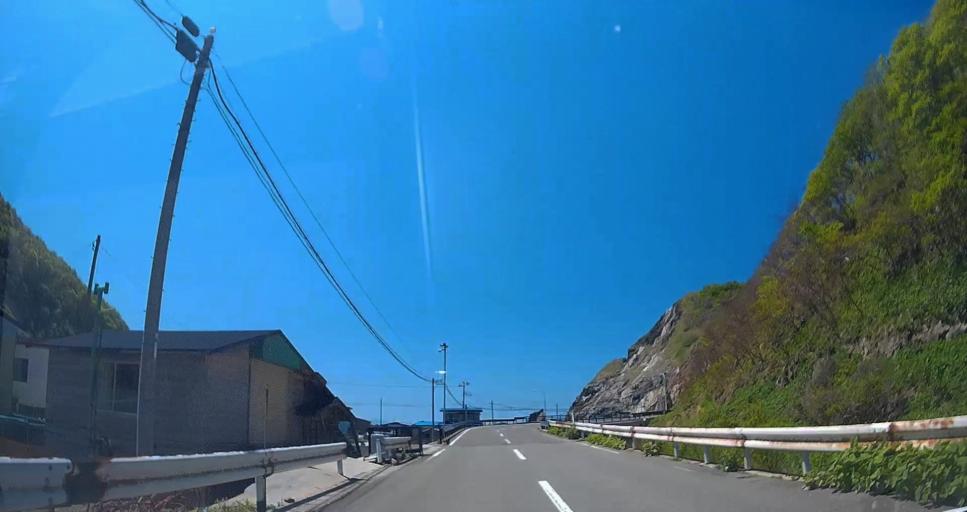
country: JP
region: Aomori
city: Mutsu
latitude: 41.3282
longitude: 140.8087
